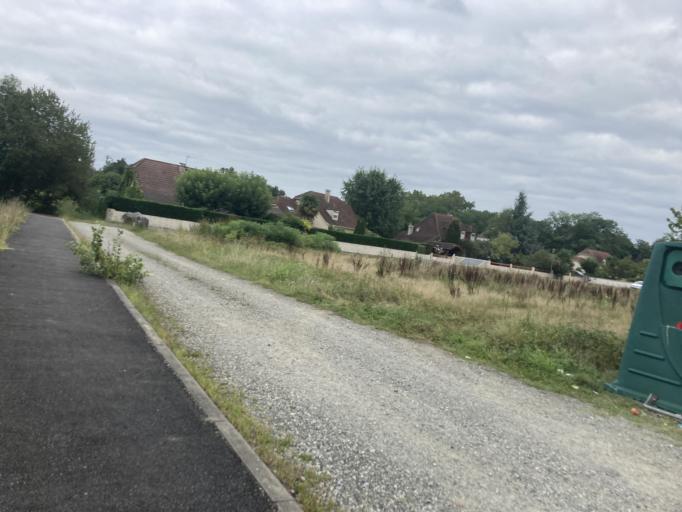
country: FR
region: Aquitaine
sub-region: Departement des Pyrenees-Atlantiques
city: Arbus
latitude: 43.3245
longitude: -0.4900
